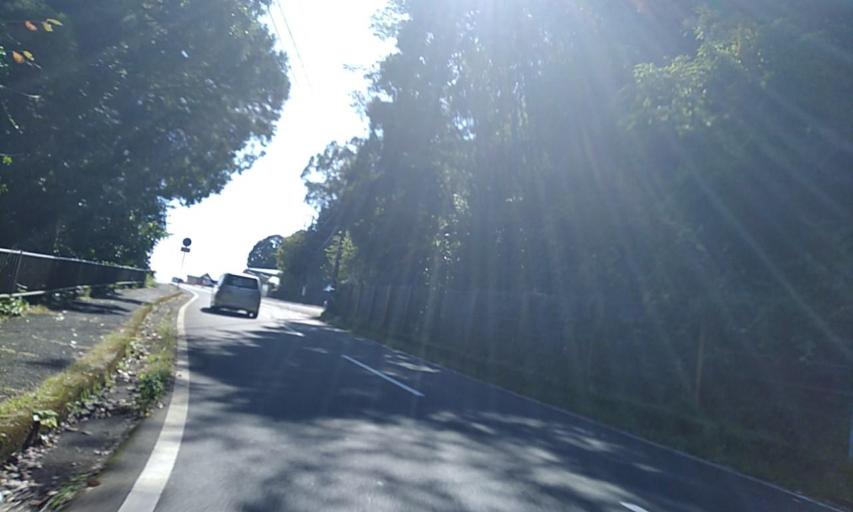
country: JP
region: Mie
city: Owase
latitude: 33.8935
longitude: 136.1147
